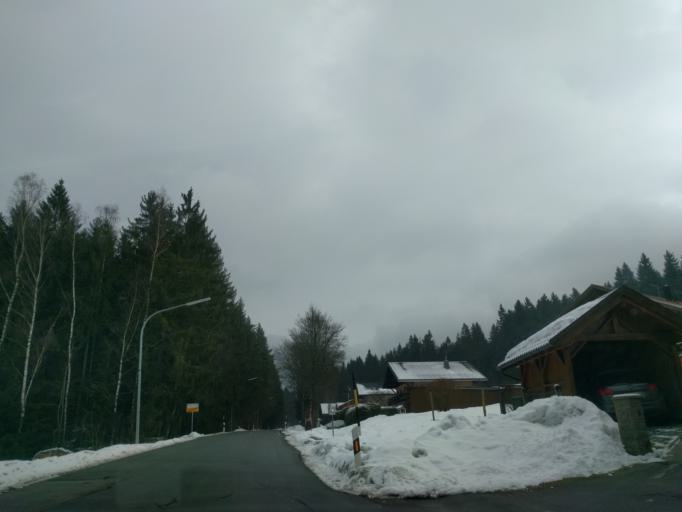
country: DE
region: Bavaria
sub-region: Lower Bavaria
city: Lindberg
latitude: 49.0489
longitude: 13.2648
